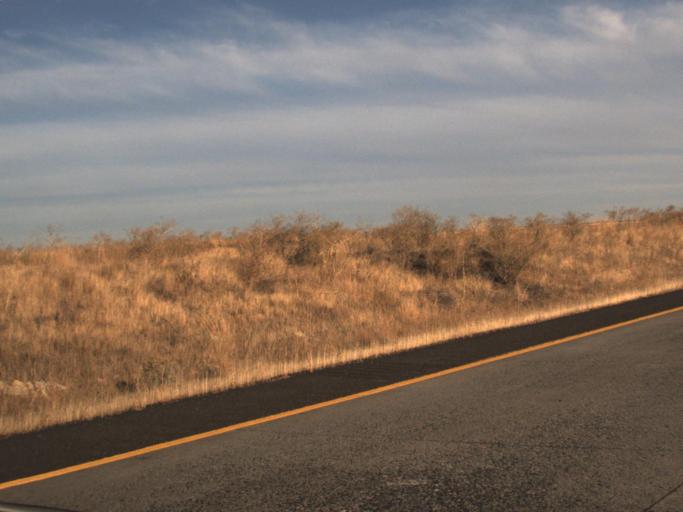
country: US
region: Washington
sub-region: Franklin County
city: Connell
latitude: 46.7135
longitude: -118.8359
